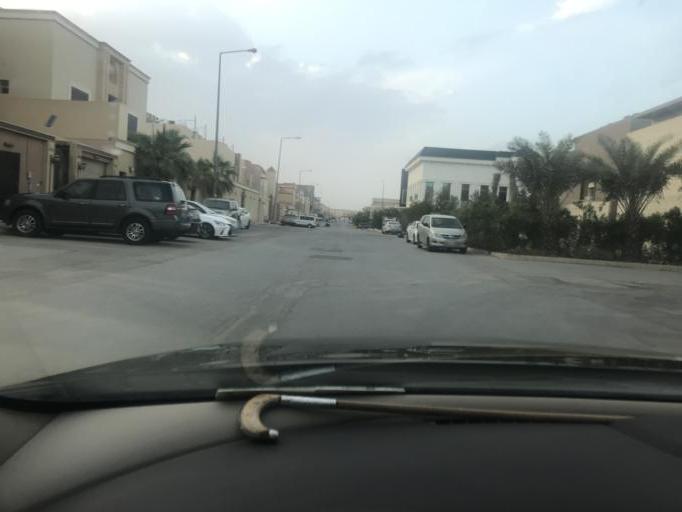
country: SA
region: Ar Riyad
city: Riyadh
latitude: 24.7295
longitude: 46.7448
